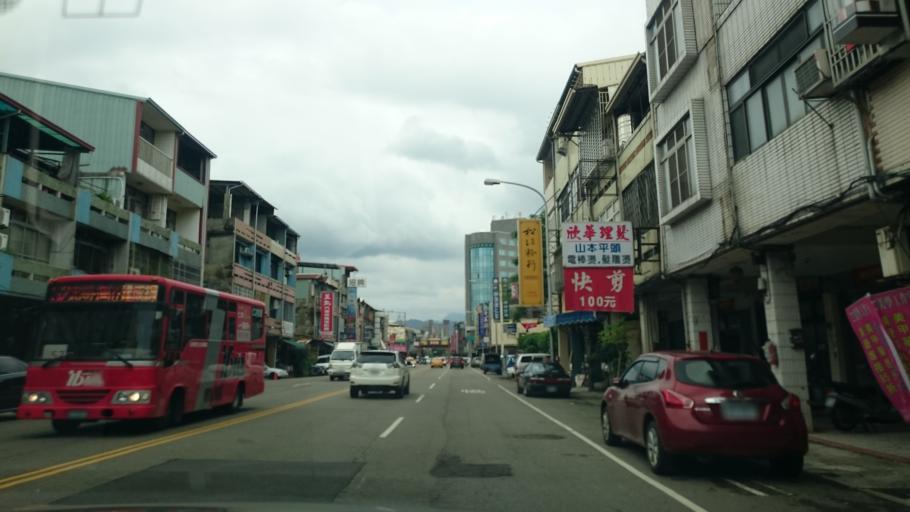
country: TW
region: Taiwan
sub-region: Taichung City
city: Taichung
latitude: 24.1427
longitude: 120.6928
